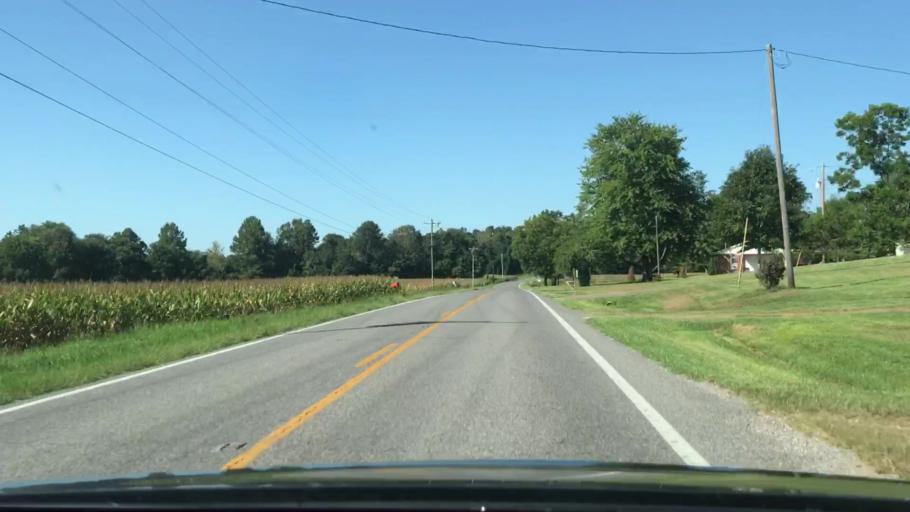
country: US
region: Kentucky
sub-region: Graves County
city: Mayfield
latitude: 36.7695
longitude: -88.5632
